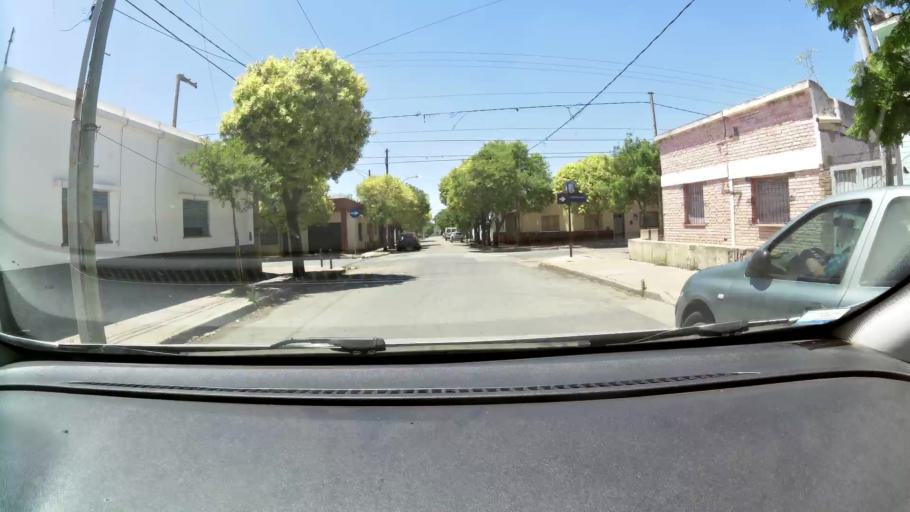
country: AR
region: Cordoba
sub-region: Departamento de Capital
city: Cordoba
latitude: -31.3844
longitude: -64.1327
